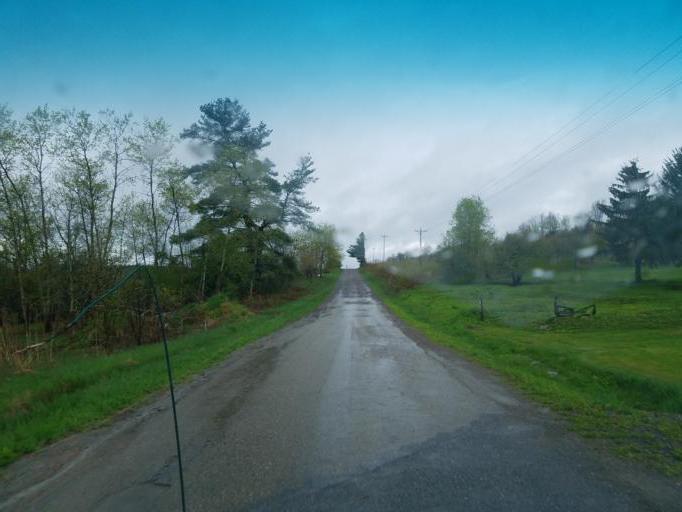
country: US
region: Pennsylvania
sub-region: Tioga County
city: Westfield
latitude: 41.9784
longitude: -77.6807
